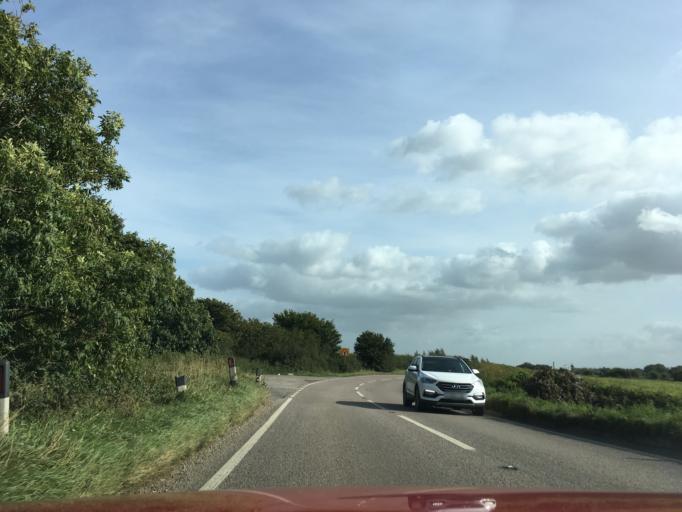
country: GB
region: England
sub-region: South Gloucestershire
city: Charfield
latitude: 51.6156
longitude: -2.4148
